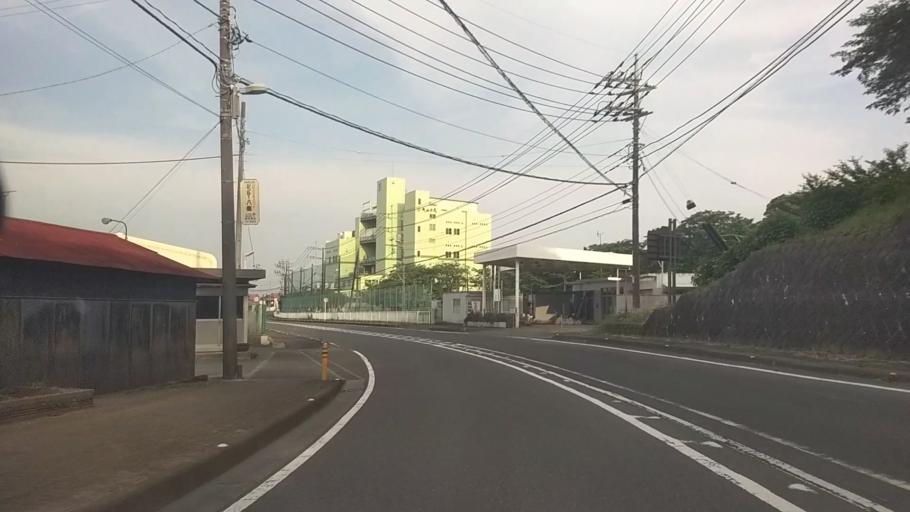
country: JP
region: Kanagawa
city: Odawara
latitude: 35.3485
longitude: 139.0943
